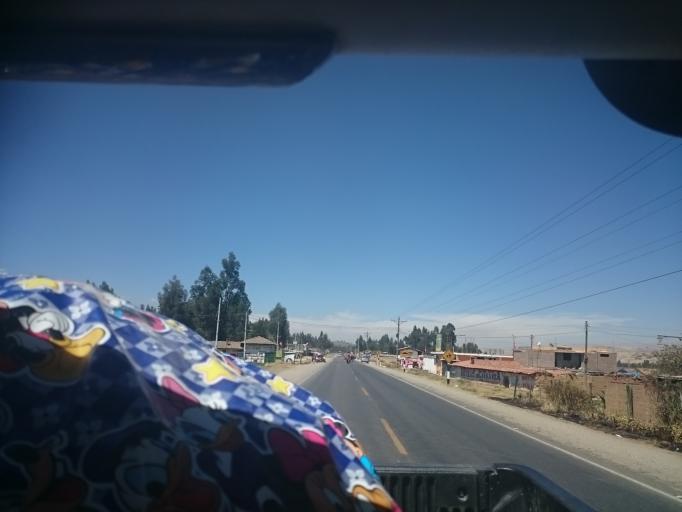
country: PE
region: Junin
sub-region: Provincia de Jauja
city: San Lorenzo
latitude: -11.8467
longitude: -75.3858
